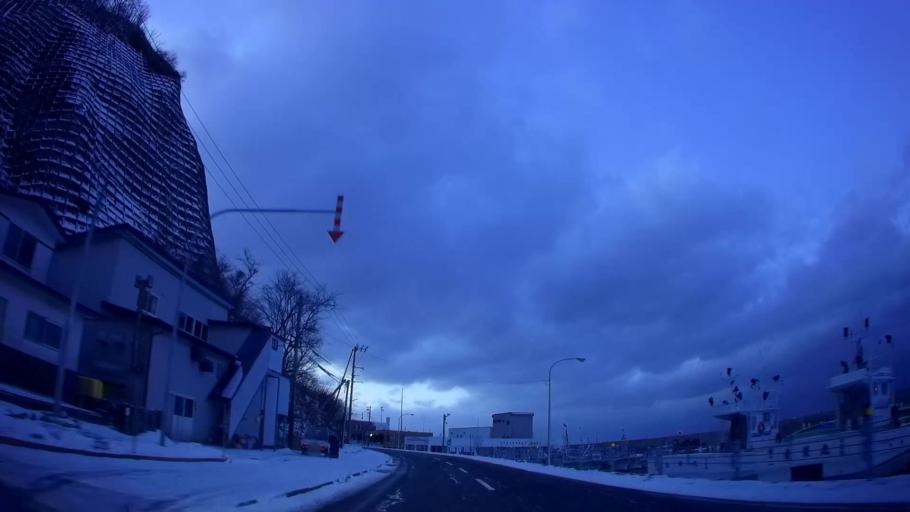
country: JP
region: Hokkaido
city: Hakodate
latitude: 41.8872
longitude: 141.0669
